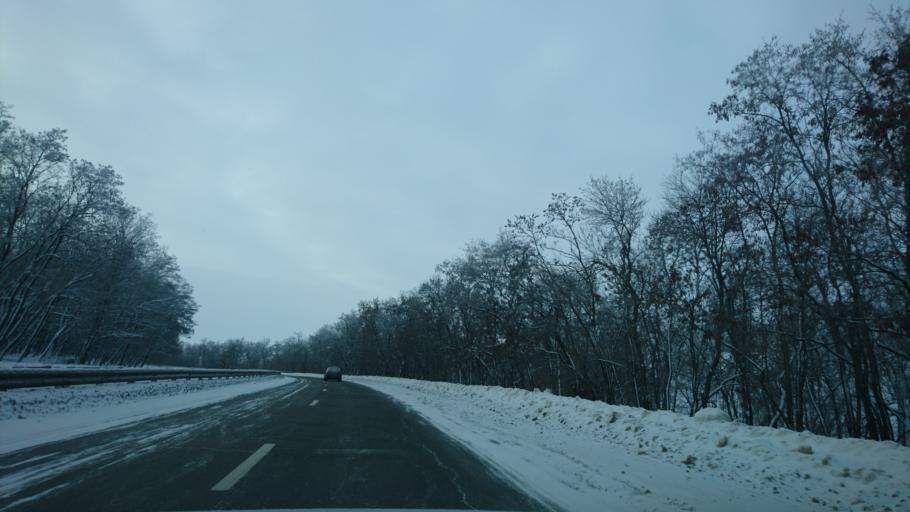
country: RU
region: Belgorod
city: Mayskiy
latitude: 50.4837
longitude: 36.4081
